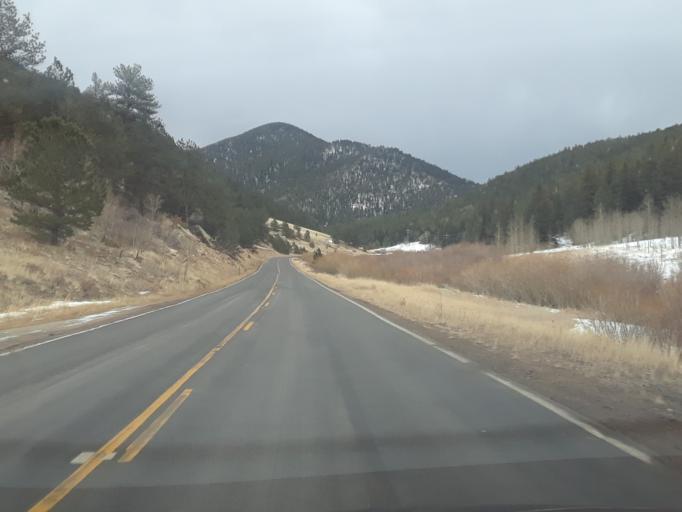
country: US
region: Colorado
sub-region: Boulder County
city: Coal Creek
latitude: 39.8326
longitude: -105.4270
